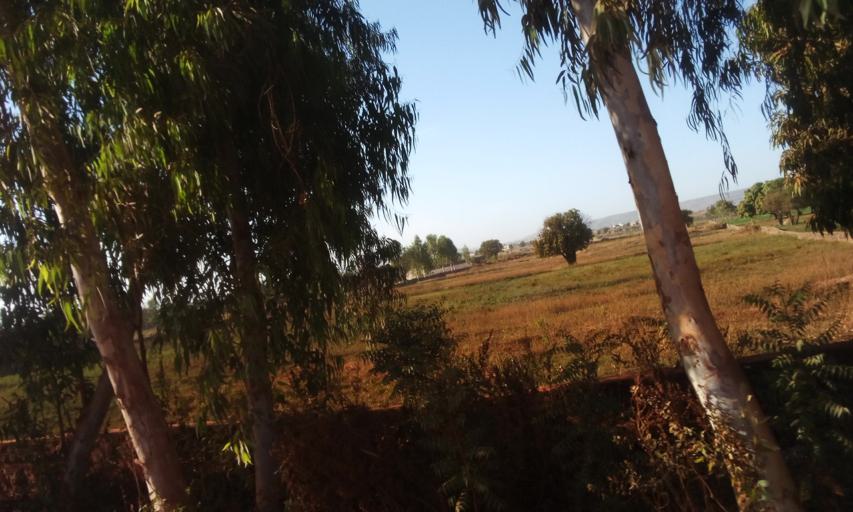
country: ML
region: Bamako
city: Bamako
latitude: 12.6416
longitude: -7.9080
